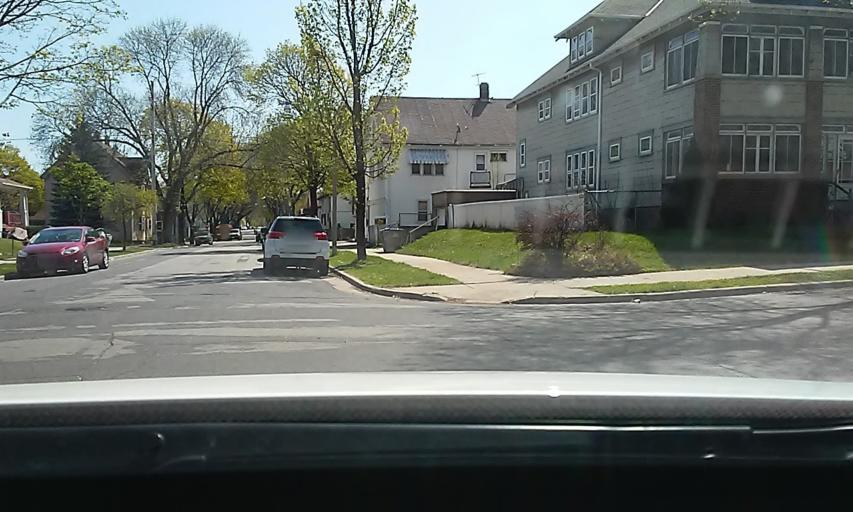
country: US
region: Wisconsin
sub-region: Milwaukee County
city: West Milwaukee
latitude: 43.0085
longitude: -87.9518
